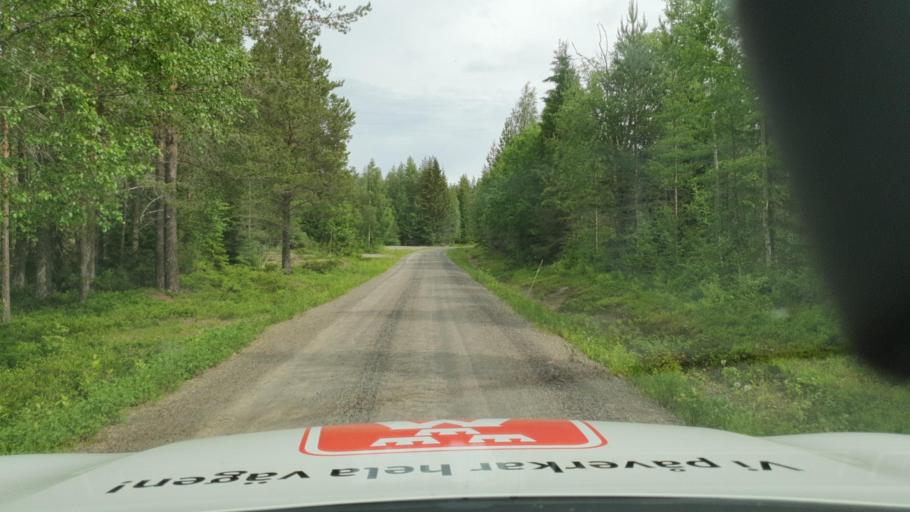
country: SE
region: Vaesterbotten
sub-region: Robertsfors Kommun
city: Robertsfors
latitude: 64.2622
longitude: 20.6627
